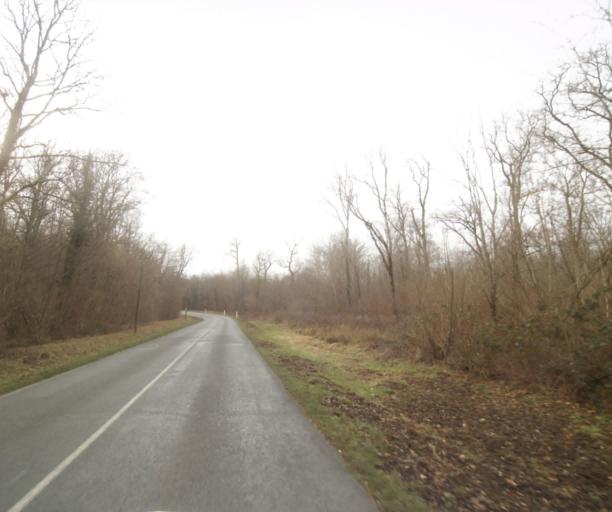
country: FR
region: Champagne-Ardenne
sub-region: Departement de la Haute-Marne
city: Villiers-en-Lieu
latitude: 48.6960
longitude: 4.8935
